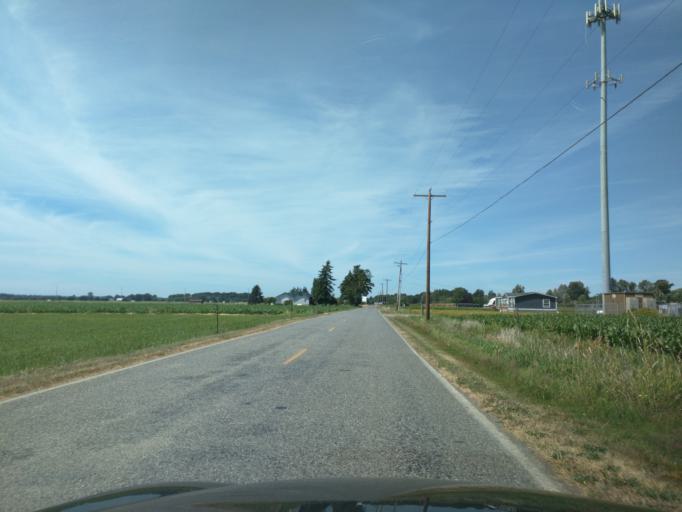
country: US
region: Washington
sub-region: Whatcom County
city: Lynden
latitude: 48.9350
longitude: -122.4321
